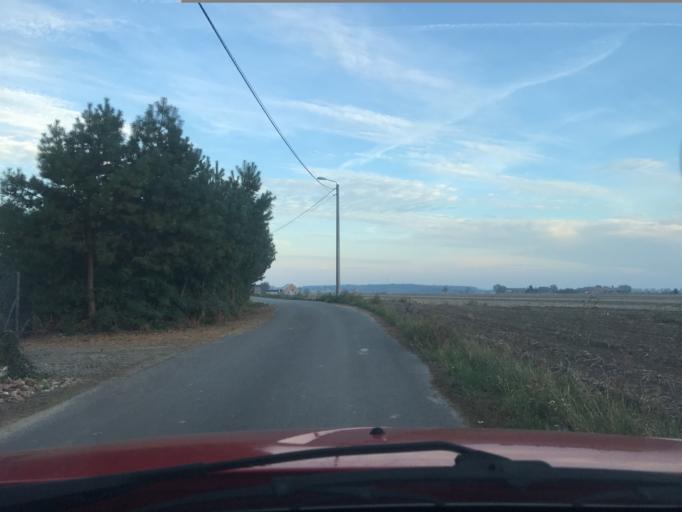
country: PL
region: Greater Poland Voivodeship
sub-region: Powiat ostrowski
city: Skalmierzyce
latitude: 51.7570
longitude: 17.9024
